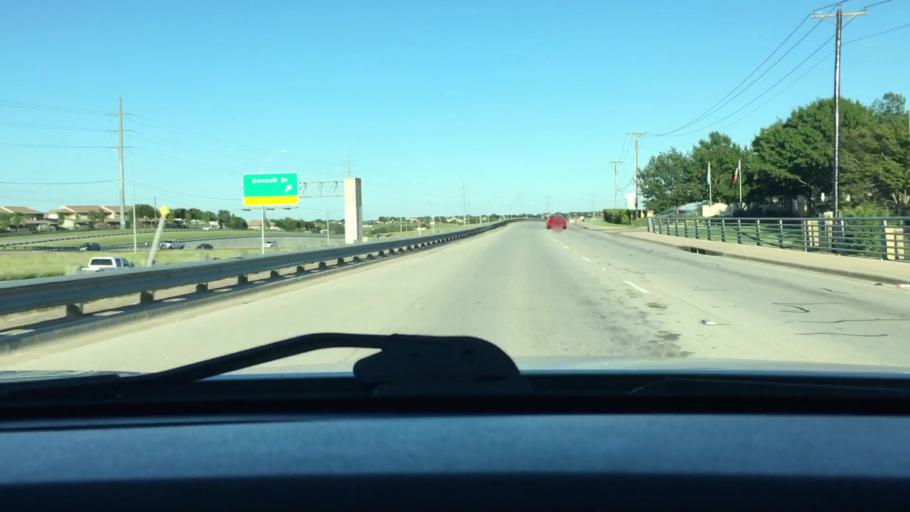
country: US
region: Virginia
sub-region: Fairfax County
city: Jefferson
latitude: 38.8672
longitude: -77.1894
